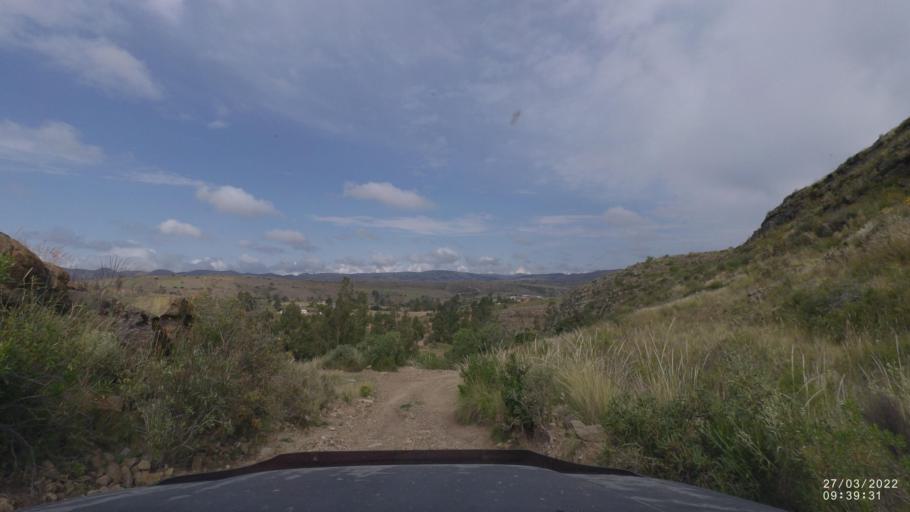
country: BO
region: Cochabamba
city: Cliza
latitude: -17.7501
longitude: -65.8979
